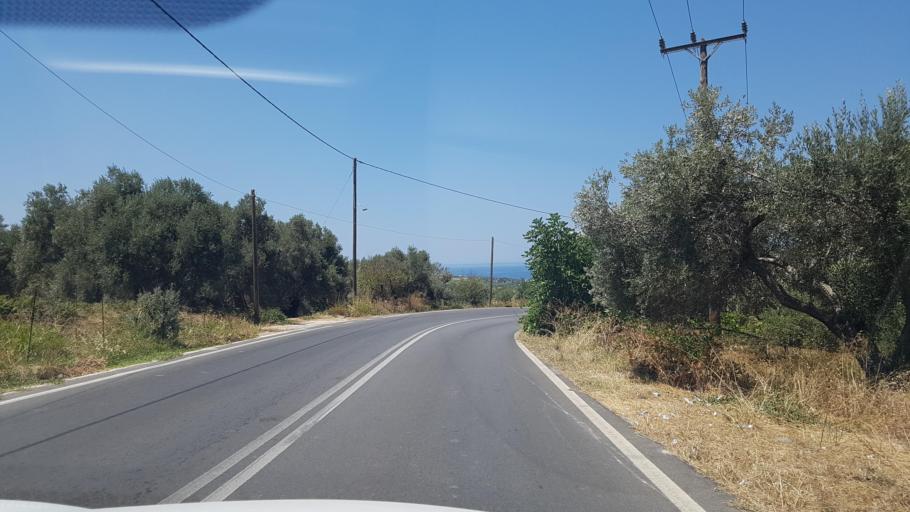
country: GR
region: Crete
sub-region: Nomos Rethymnis
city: Agia Foteini
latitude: 35.3517
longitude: 24.5897
